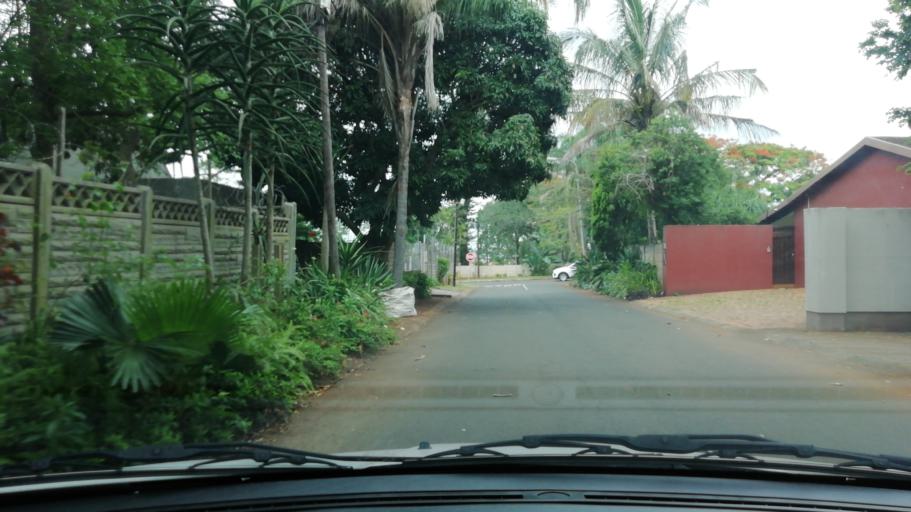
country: ZA
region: KwaZulu-Natal
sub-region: uThungulu District Municipality
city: Empangeni
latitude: -28.7503
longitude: 31.8938
